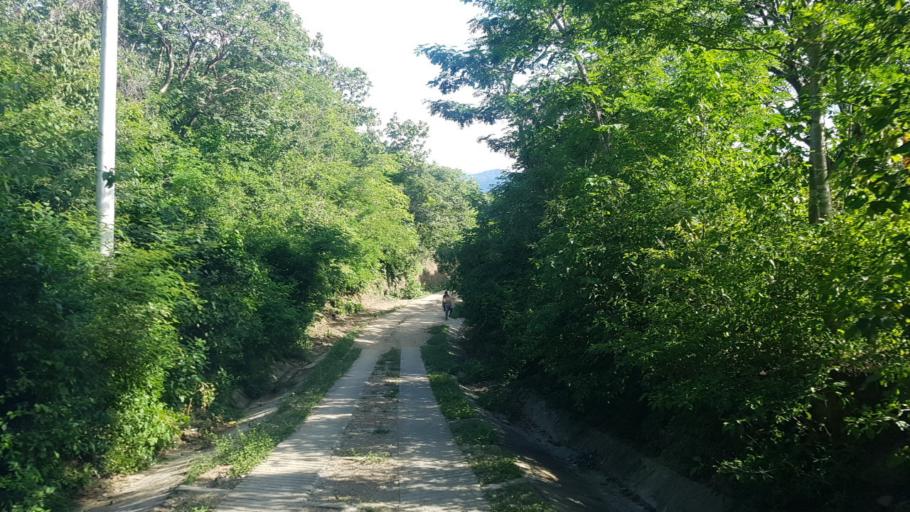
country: NI
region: Nueva Segovia
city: Mozonte
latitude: 13.6440
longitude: -86.3977
